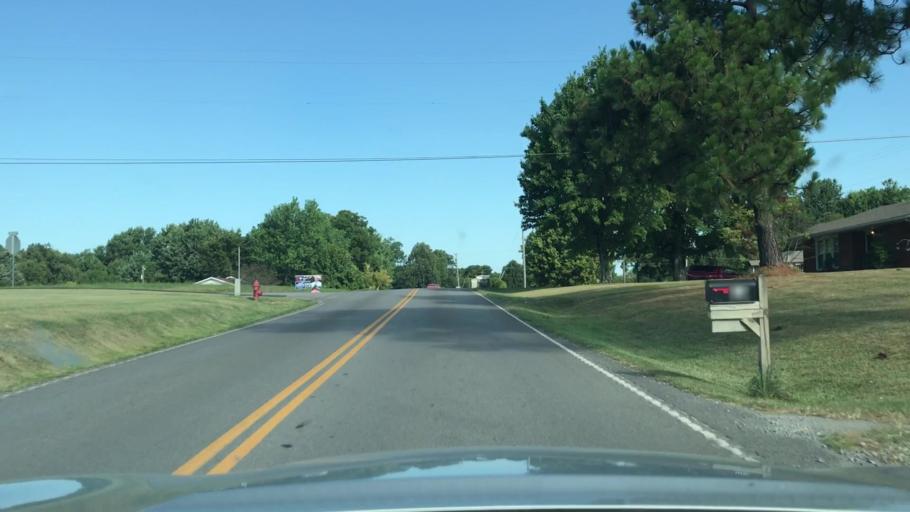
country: US
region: Kentucky
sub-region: Muhlenberg County
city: Greenville
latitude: 37.1882
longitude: -87.1681
